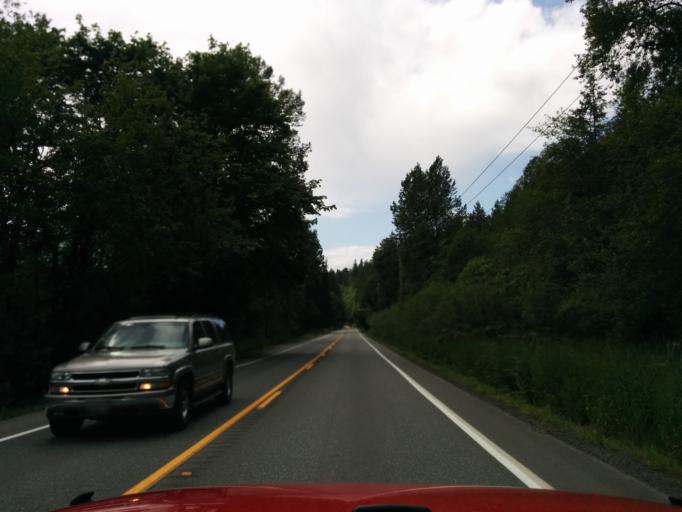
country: US
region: Washington
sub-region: King County
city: Ames Lake
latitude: 47.6270
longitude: -121.9802
